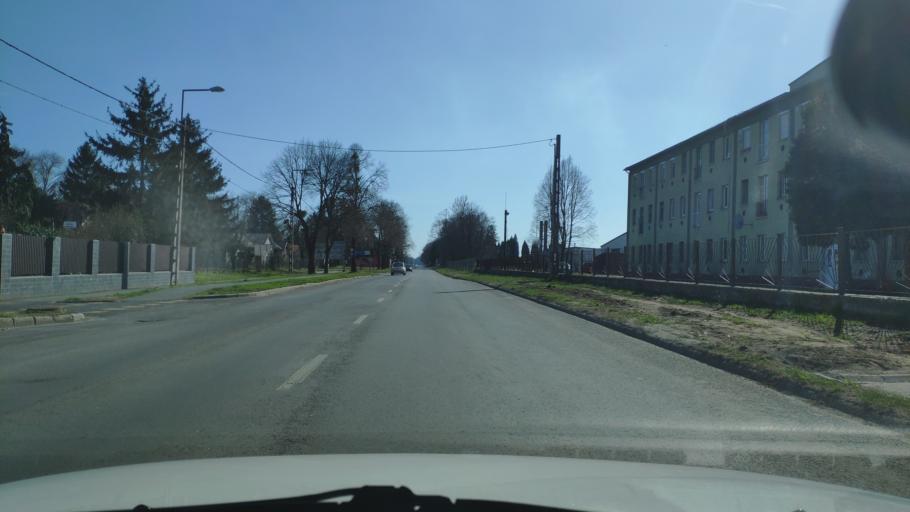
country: HU
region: Zala
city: Nagykanizsa
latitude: 46.4303
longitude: 16.9872
